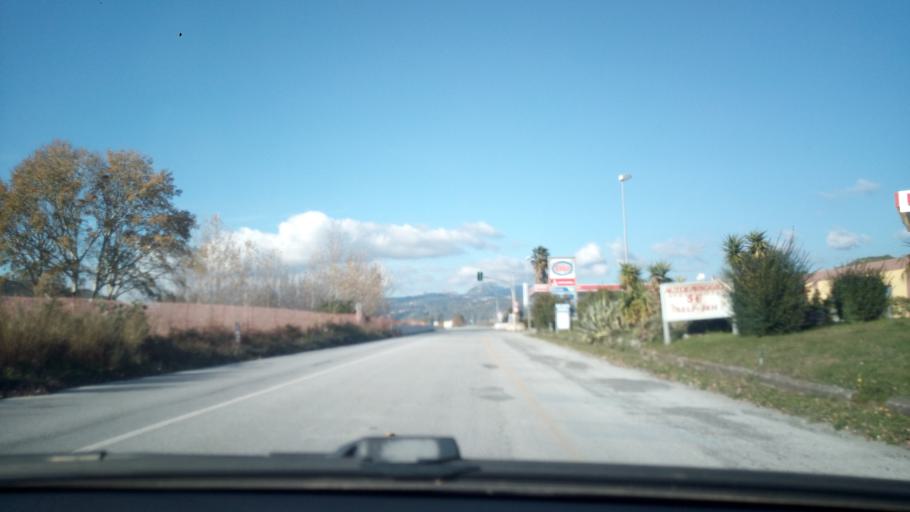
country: IT
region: Calabria
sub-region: Provincia di Catanzaro
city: Catanzaro
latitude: 38.8610
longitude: 16.5679
